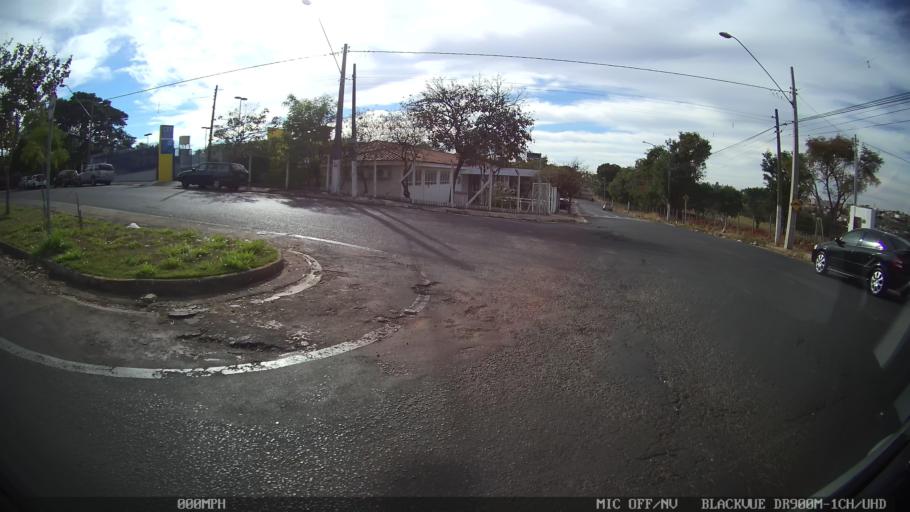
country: BR
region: Sao Paulo
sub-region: Catanduva
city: Catanduva
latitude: -21.1327
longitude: -48.9952
